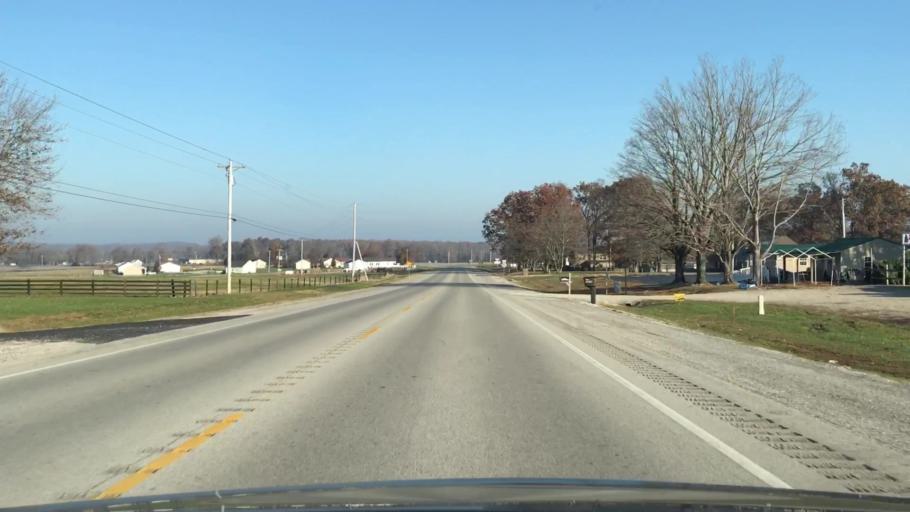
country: US
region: Kentucky
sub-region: Edmonson County
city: Brownsville
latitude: 37.1108
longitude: -86.2292
